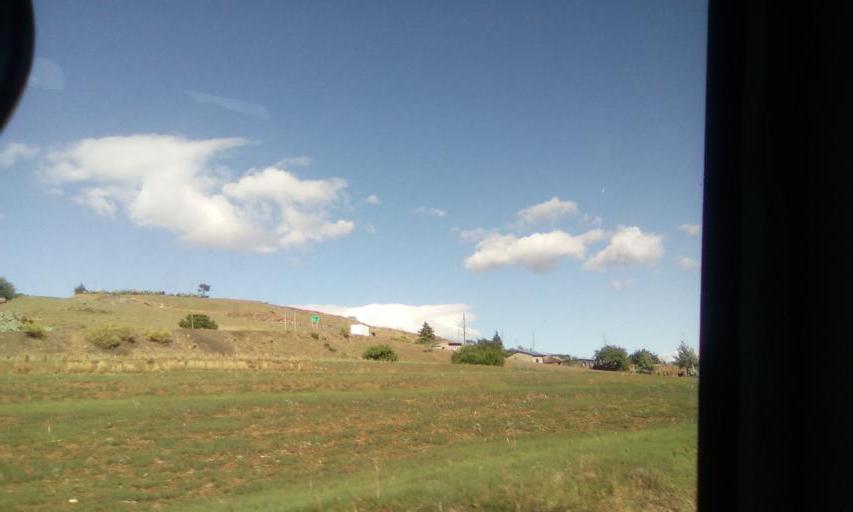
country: LS
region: Qacha's Nek
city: Qacha's Nek
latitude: -30.0510
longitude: 28.2837
